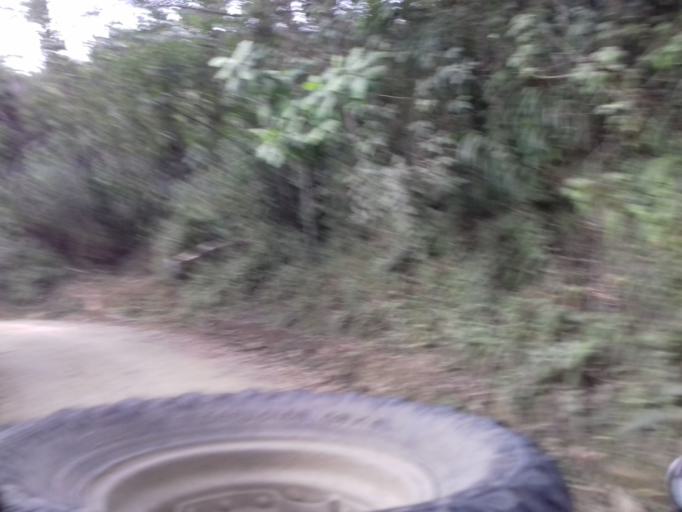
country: CO
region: Quindio
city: Salento
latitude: 4.6339
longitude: -75.5600
